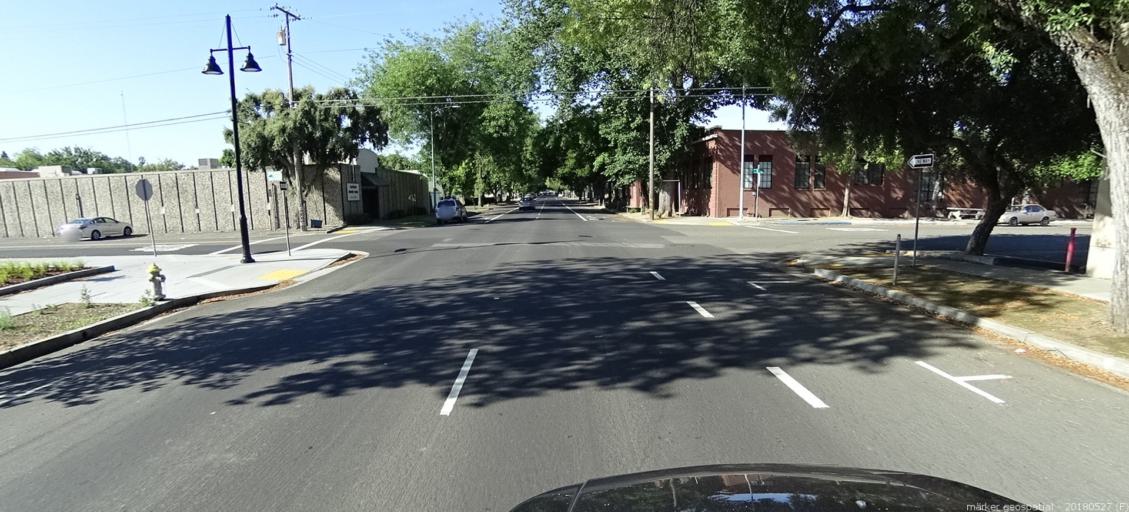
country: US
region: California
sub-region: Sacramento County
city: Sacramento
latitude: 38.5721
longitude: -121.4985
